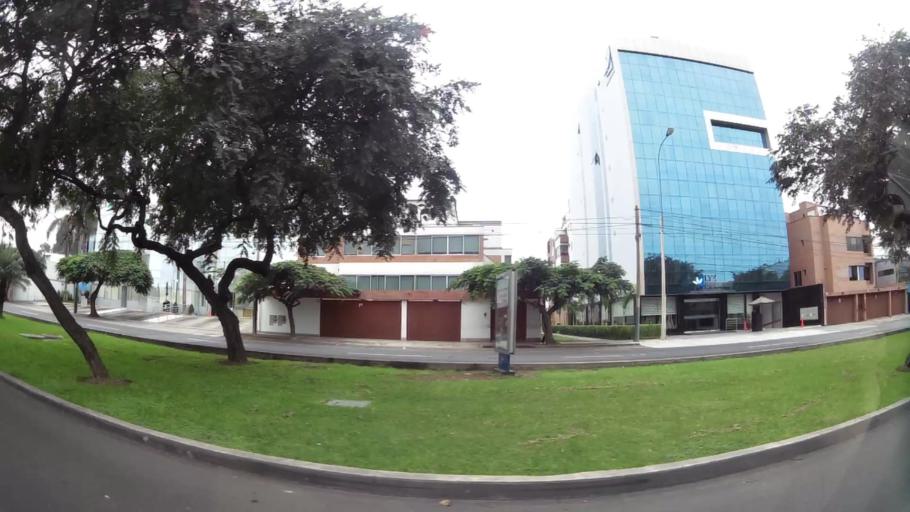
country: PE
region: Lima
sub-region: Lima
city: San Luis
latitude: -12.0955
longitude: -77.0108
